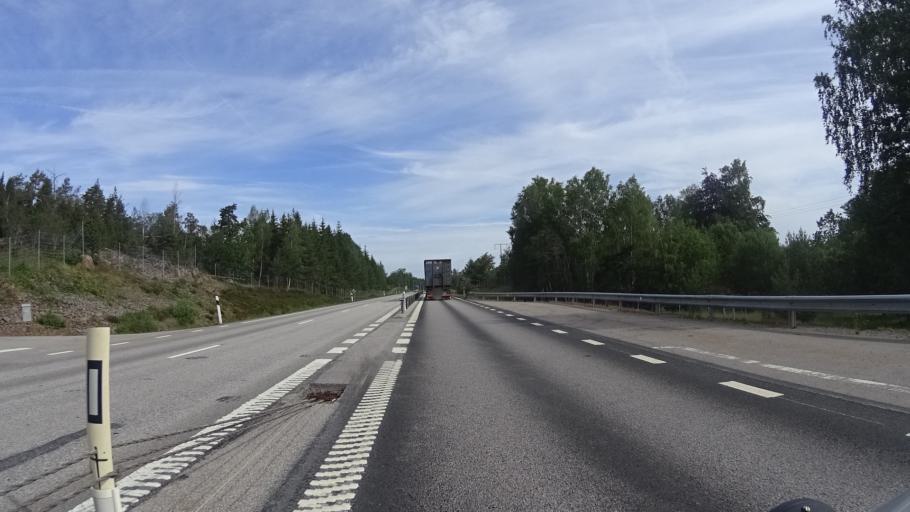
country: SE
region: Kalmar
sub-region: Vasterviks Kommun
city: Vaestervik
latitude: 57.7557
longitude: 16.5571
